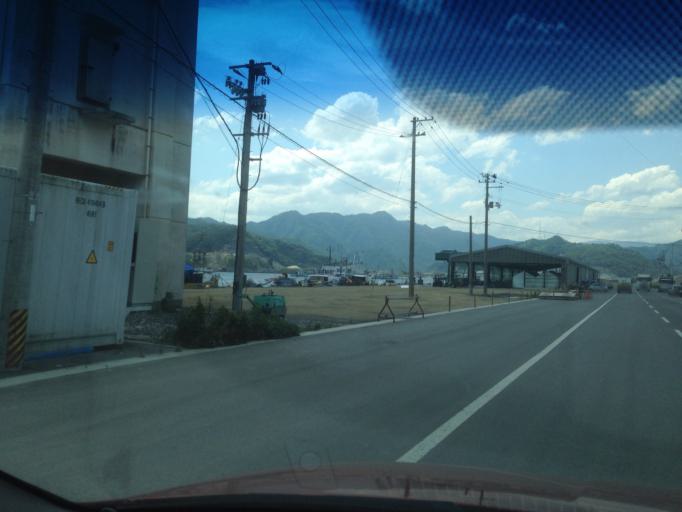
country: JP
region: Iwate
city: Otsuchi
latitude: 39.3539
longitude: 141.9249
